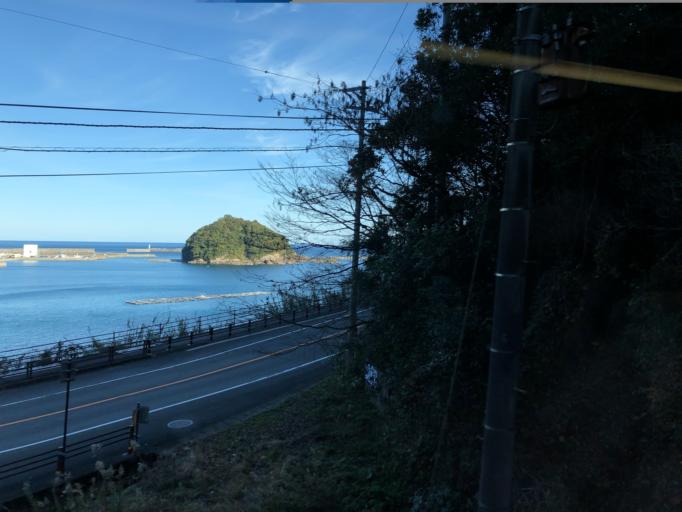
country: JP
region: Kochi
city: Nakamura
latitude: 33.0706
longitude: 133.1043
